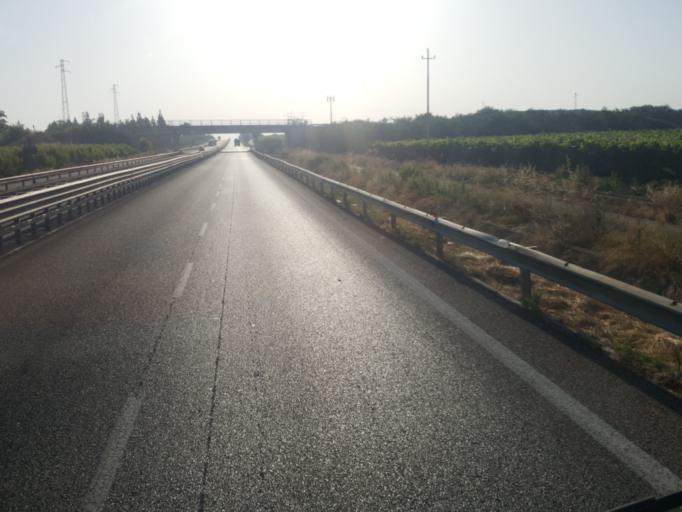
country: IT
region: Apulia
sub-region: Provincia di Foggia
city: Cerignola
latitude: 41.2742
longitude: 15.9683
